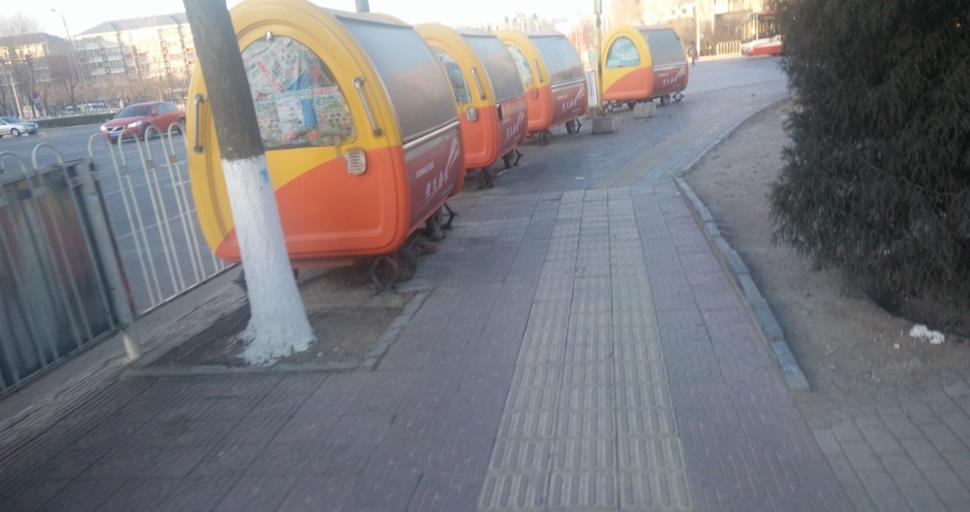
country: CN
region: Beijing
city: Jiugong
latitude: 39.7611
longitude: 116.4975
